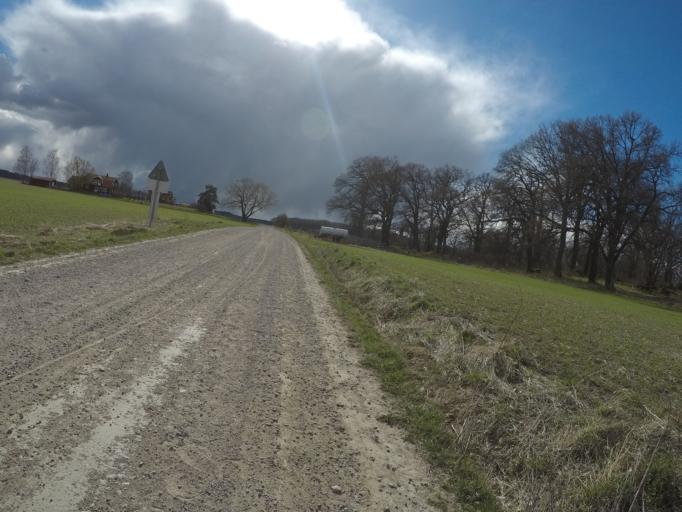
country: SE
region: Vaestmanland
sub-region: Hallstahammars Kommun
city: Kolback
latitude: 59.5187
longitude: 16.2433
